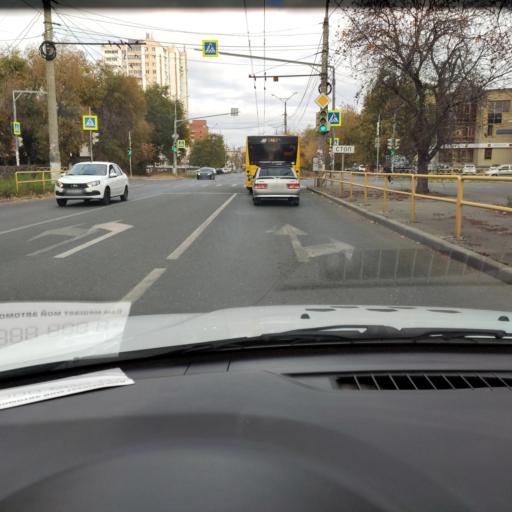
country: RU
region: Samara
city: Tol'yatti
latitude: 53.5185
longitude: 49.4161
